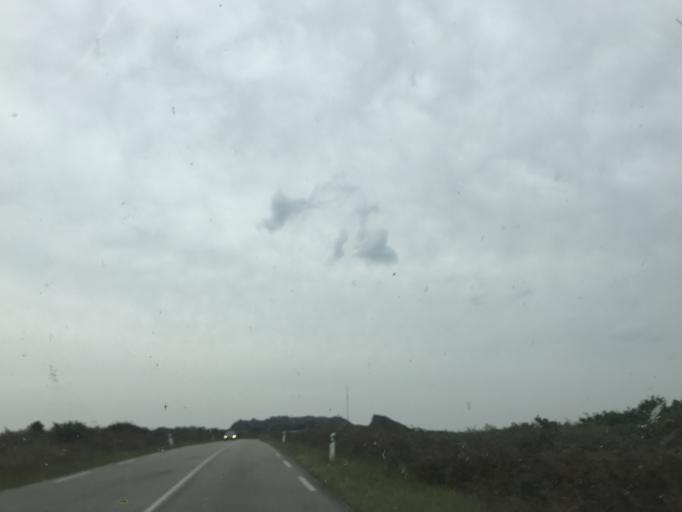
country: FR
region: Brittany
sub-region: Departement du Finistere
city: Plouneour-Menez
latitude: 48.4001
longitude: -3.9227
